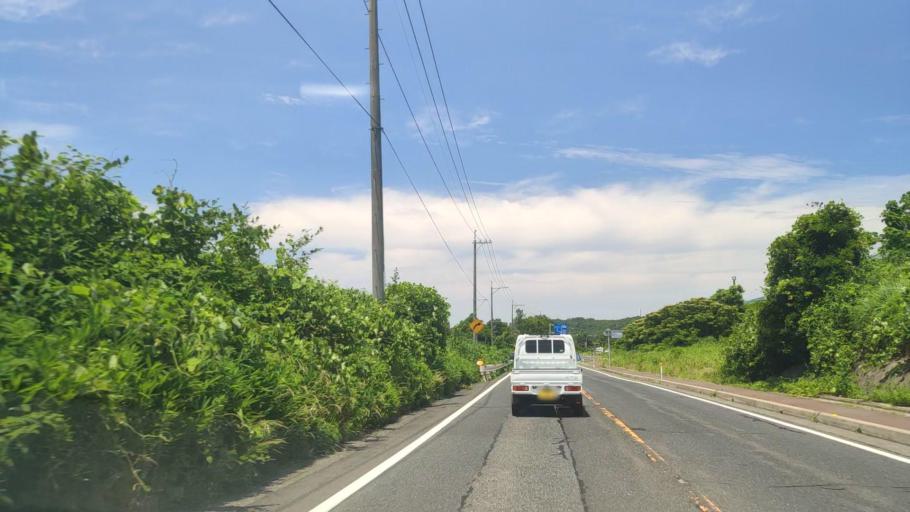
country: JP
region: Tottori
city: Tottori
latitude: 35.4392
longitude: 134.2563
